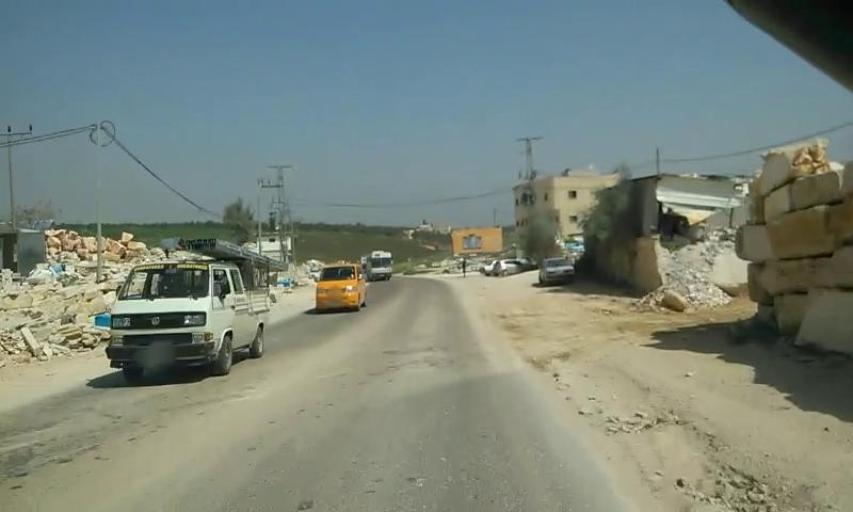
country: PS
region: West Bank
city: Ash Shuhada'
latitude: 32.4374
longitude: 35.2741
